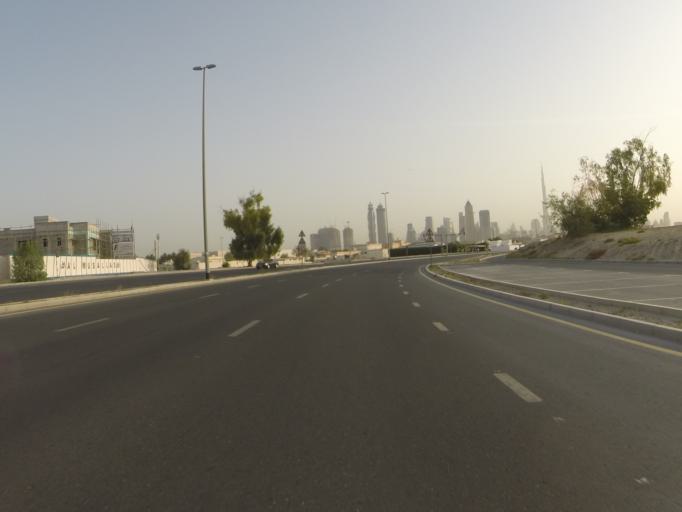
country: AE
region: Dubai
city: Dubai
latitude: 25.1615
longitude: 55.2567
